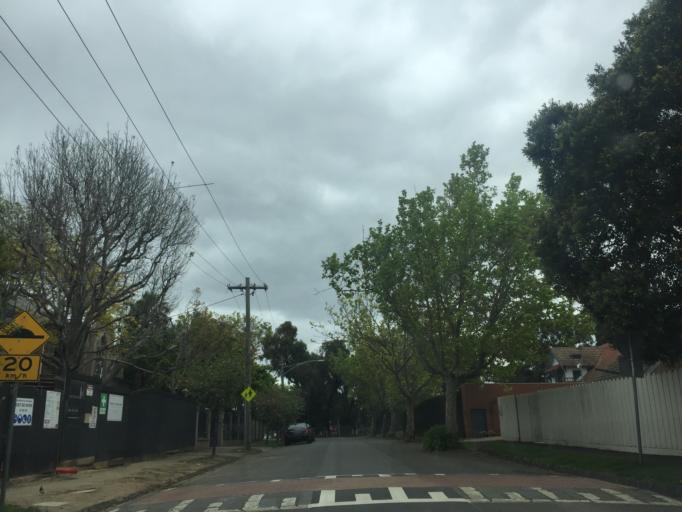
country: AU
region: Victoria
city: Balwyn
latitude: -37.8124
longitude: 145.0571
